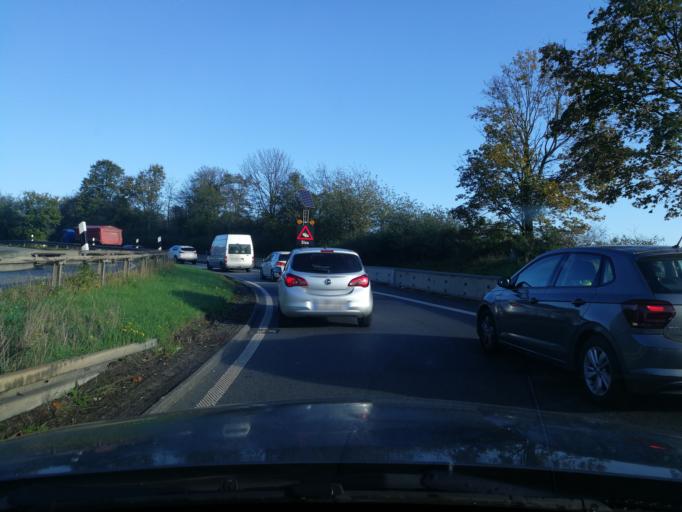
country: DE
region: North Rhine-Westphalia
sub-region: Regierungsbezirk Dusseldorf
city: Dusseldorf
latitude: 51.1633
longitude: 6.7707
